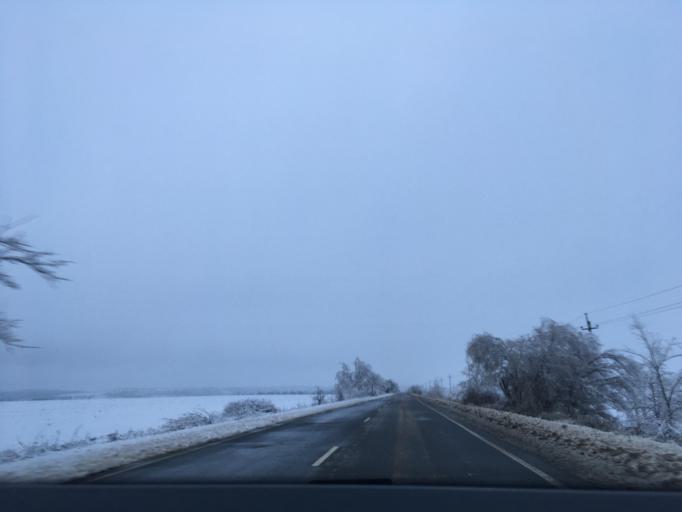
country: RU
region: Voronezj
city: Verkhniy Mamon
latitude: 50.0212
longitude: 40.1005
